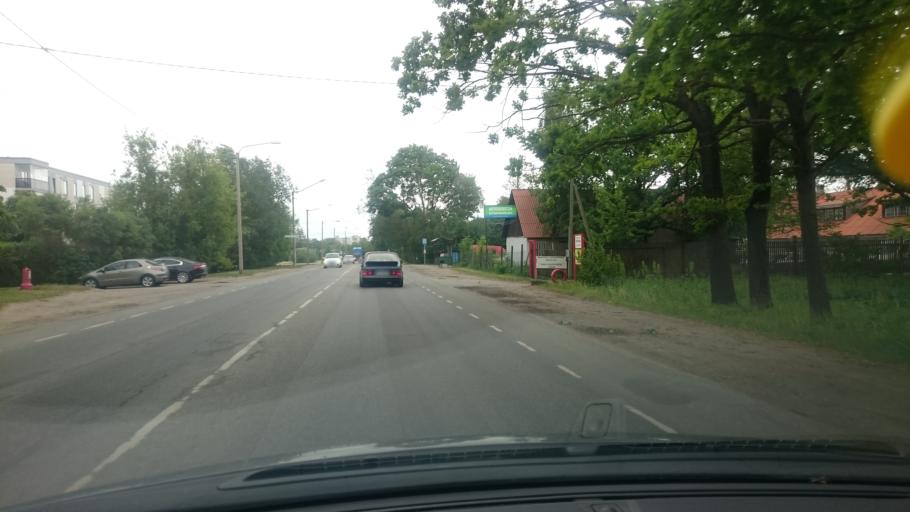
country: EE
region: Harju
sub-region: Saue vald
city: Laagri
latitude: 59.4170
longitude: 24.6365
